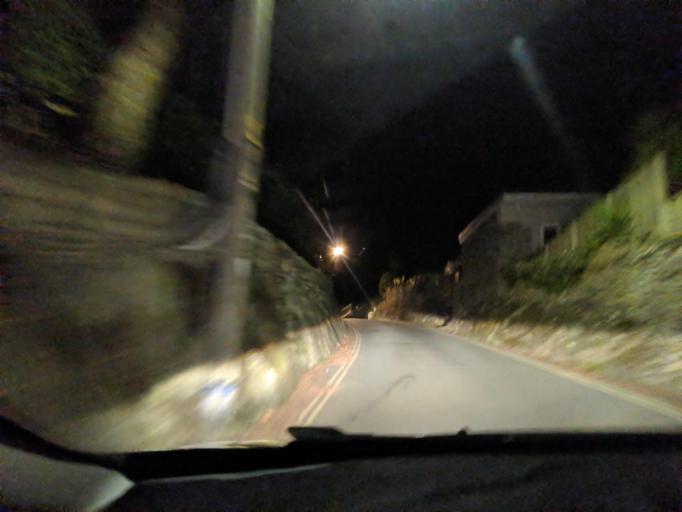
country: GB
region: England
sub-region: Cornwall
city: Mevagissey
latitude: 50.2701
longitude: -4.7907
